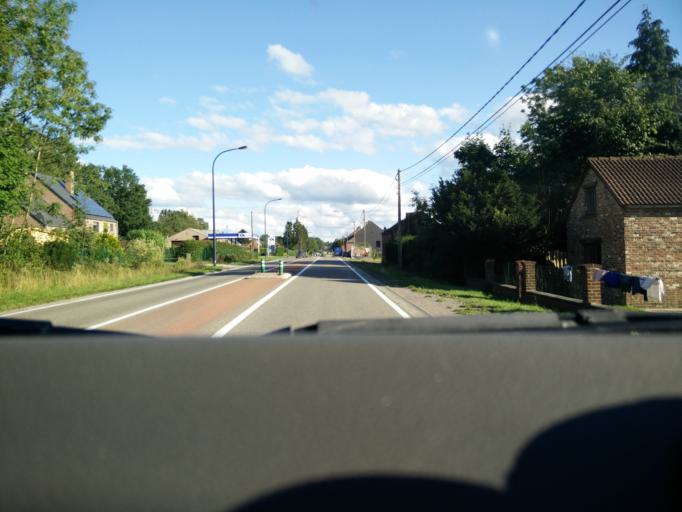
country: BE
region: Wallonia
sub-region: Province du Hainaut
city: Beaumont
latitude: 50.1820
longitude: 4.2231
